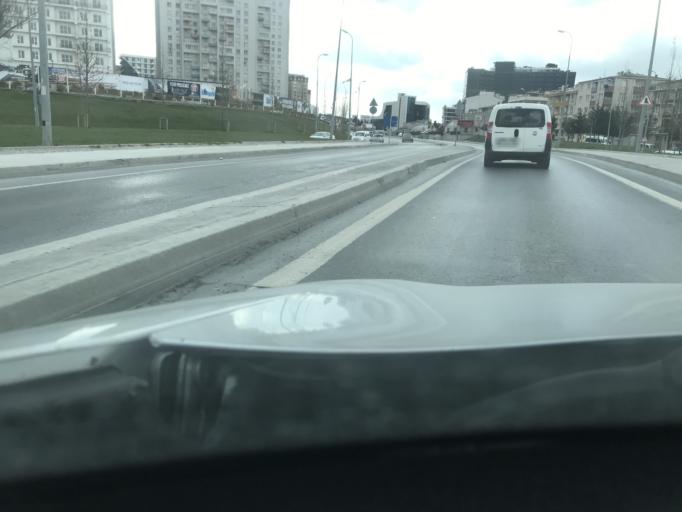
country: TR
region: Istanbul
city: Esenyurt
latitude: 41.0318
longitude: 28.6863
